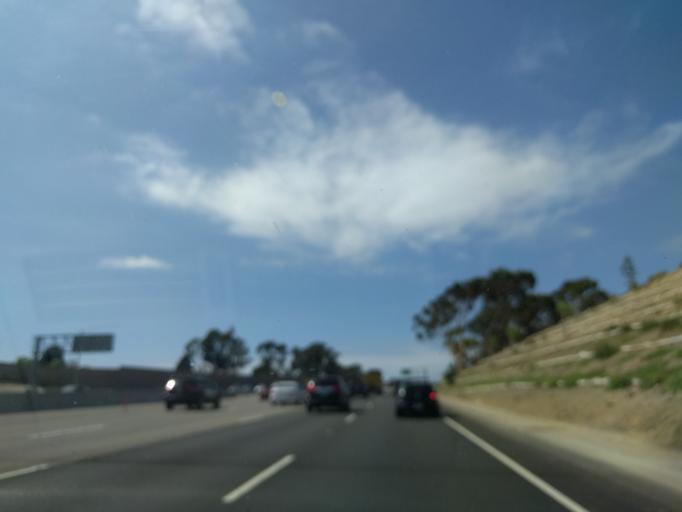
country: US
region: California
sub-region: Orange County
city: San Clemente
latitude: 33.4558
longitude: -117.6498
